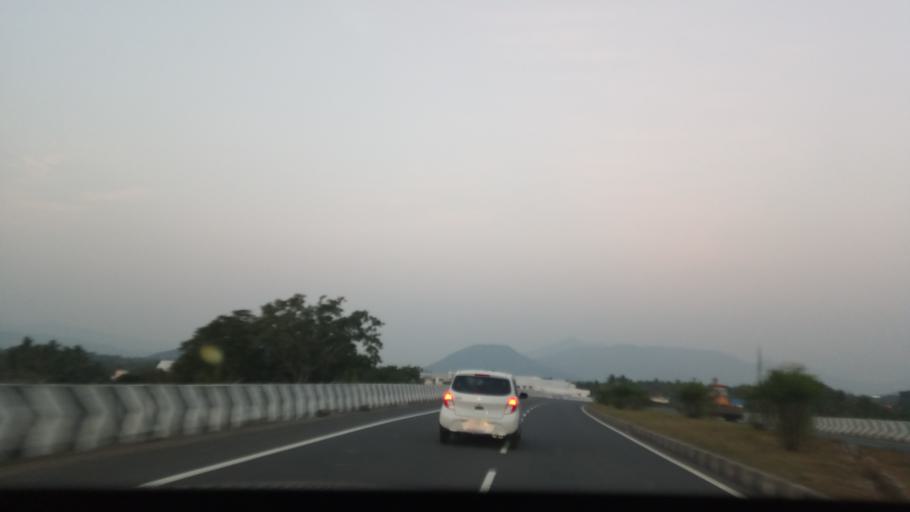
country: IN
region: Tamil Nadu
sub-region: Salem
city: Belur
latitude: 11.6559
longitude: 78.4153
